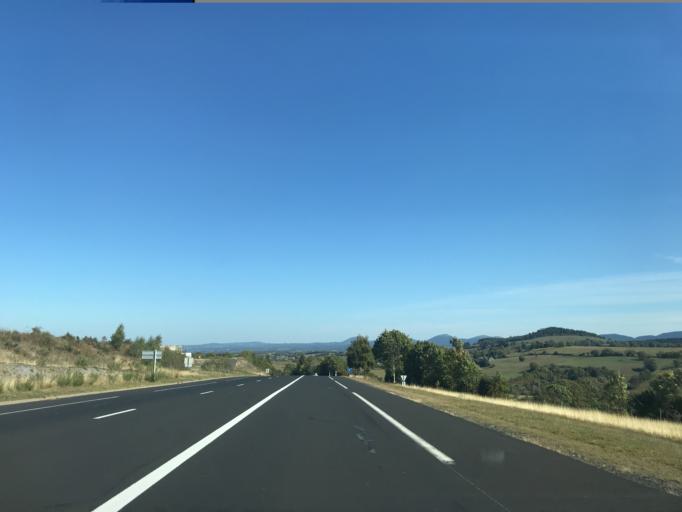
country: FR
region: Auvergne
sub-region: Departement du Puy-de-Dome
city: La Bourboule
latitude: 45.6687
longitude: 2.7858
